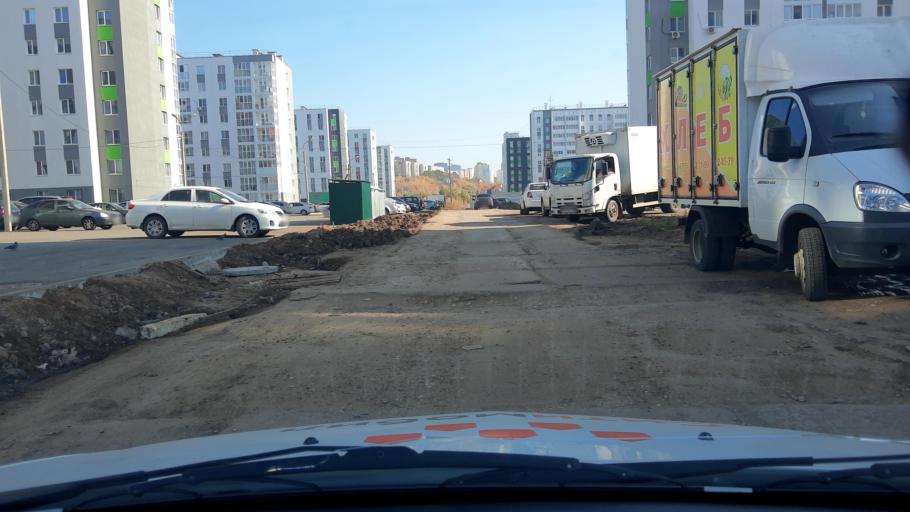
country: RU
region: Bashkortostan
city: Ufa
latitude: 54.6937
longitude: 55.9681
